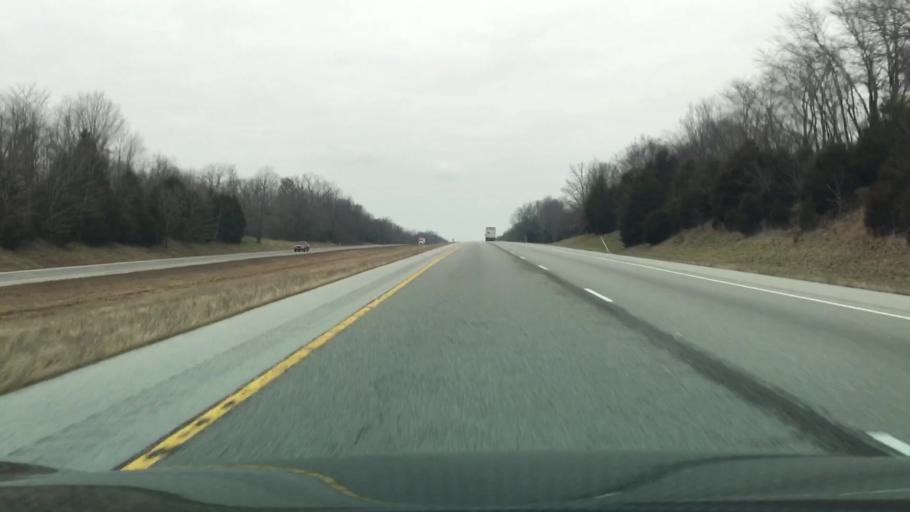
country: US
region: Illinois
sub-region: Johnson County
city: Vienna
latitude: 37.3806
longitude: -88.8210
